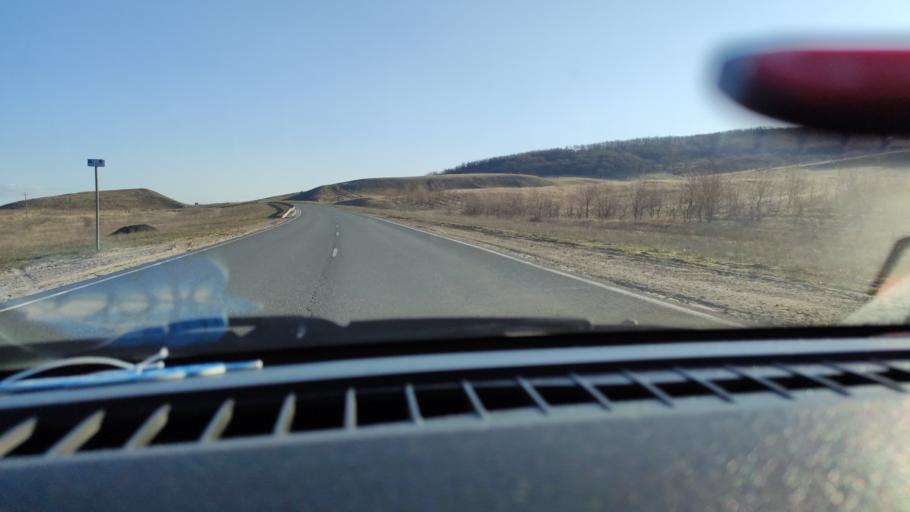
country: RU
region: Saratov
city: Alekseyevka
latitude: 52.3377
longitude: 47.9326
